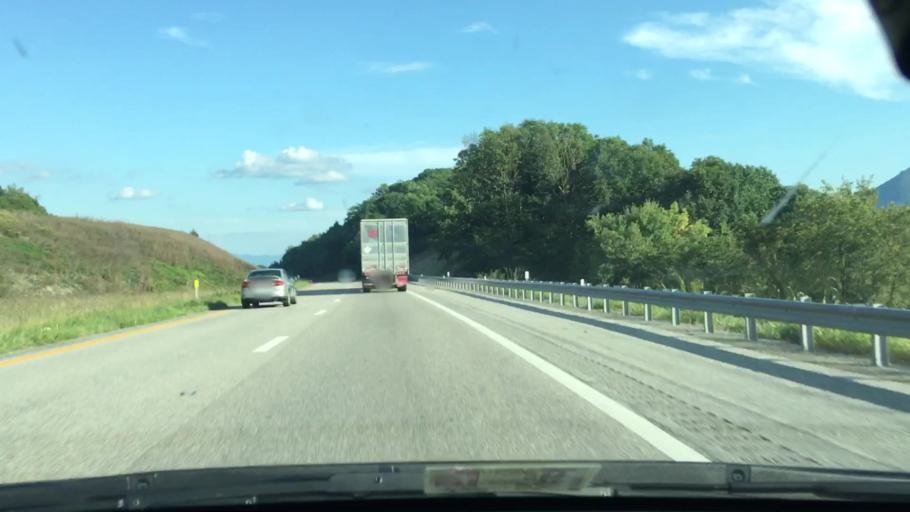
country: US
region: Virginia
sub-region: City of Lexington
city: Lexington
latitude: 37.8909
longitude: -79.5645
